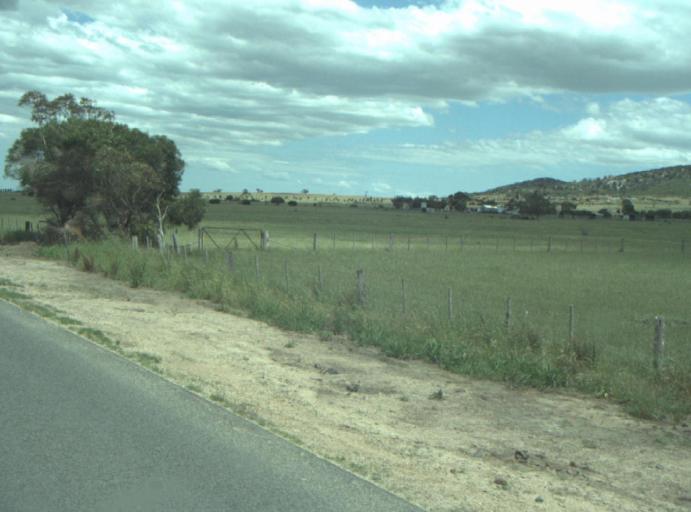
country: AU
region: Victoria
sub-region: Wyndham
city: Little River
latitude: -37.9223
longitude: 144.4638
